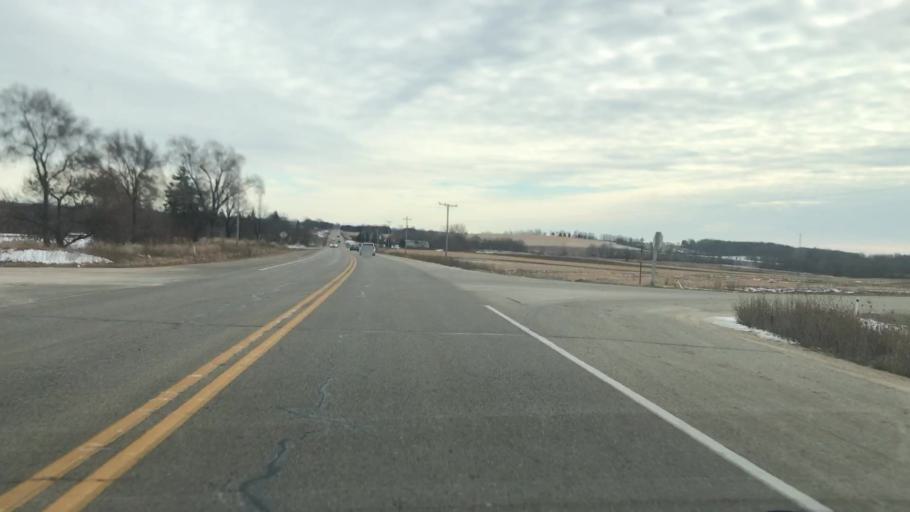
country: US
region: Wisconsin
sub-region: Dodge County
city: Theresa
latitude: 43.4292
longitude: -88.4406
